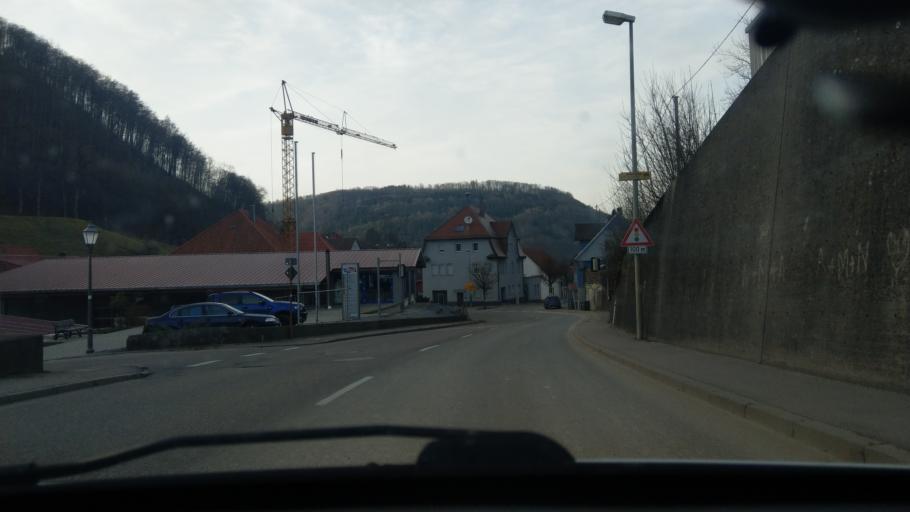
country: DE
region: Baden-Wuerttemberg
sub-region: Regierungsbezirk Stuttgart
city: Bohmenkirch
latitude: 48.7045
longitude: 9.8884
